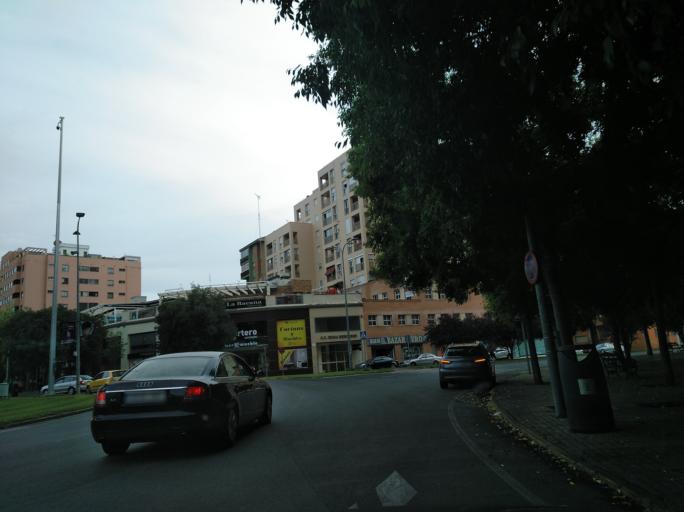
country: ES
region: Extremadura
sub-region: Provincia de Badajoz
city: Badajoz
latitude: 38.8670
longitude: -6.9864
